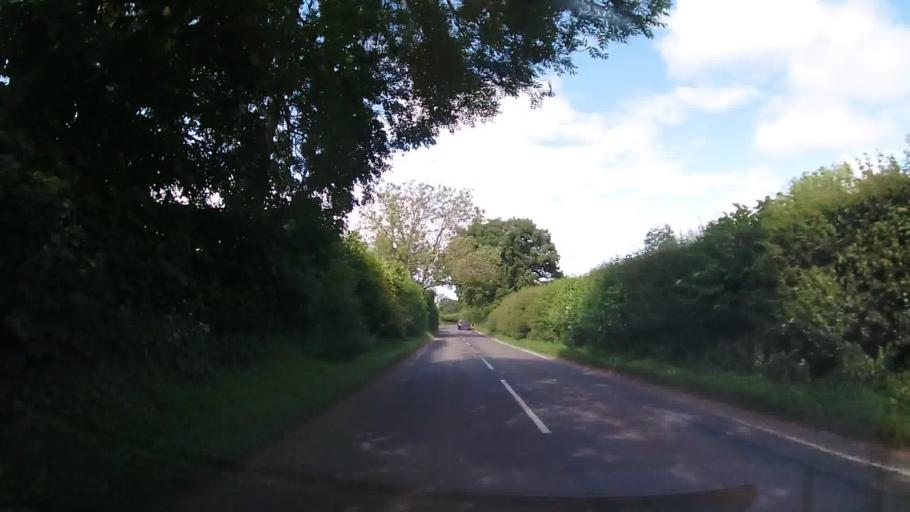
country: GB
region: England
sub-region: Shropshire
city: Petton
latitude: 52.8038
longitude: -2.8408
